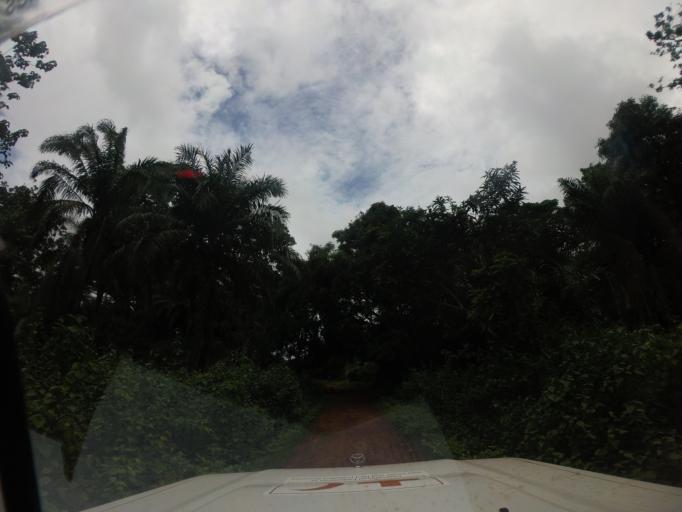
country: SL
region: Northern Province
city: Kamakwie
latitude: 9.6943
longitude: -12.2683
